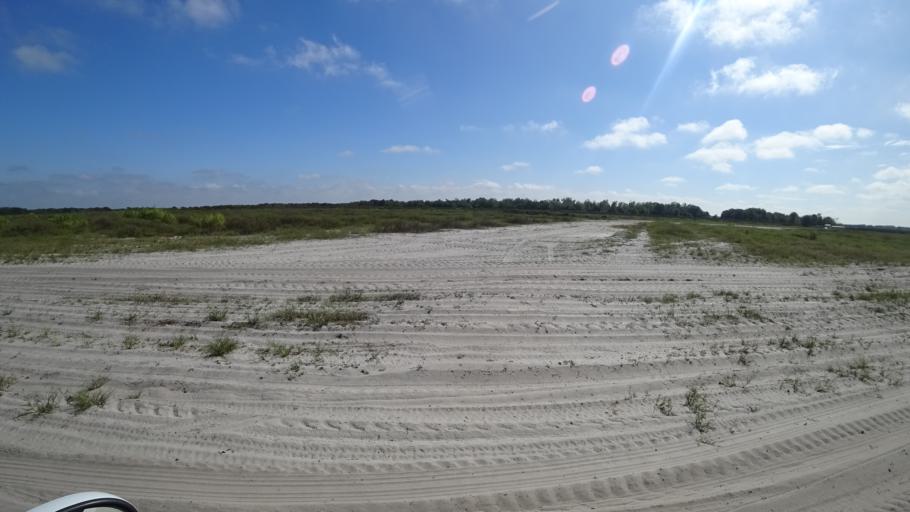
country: US
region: Florida
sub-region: DeSoto County
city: Arcadia
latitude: 27.2901
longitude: -82.0774
